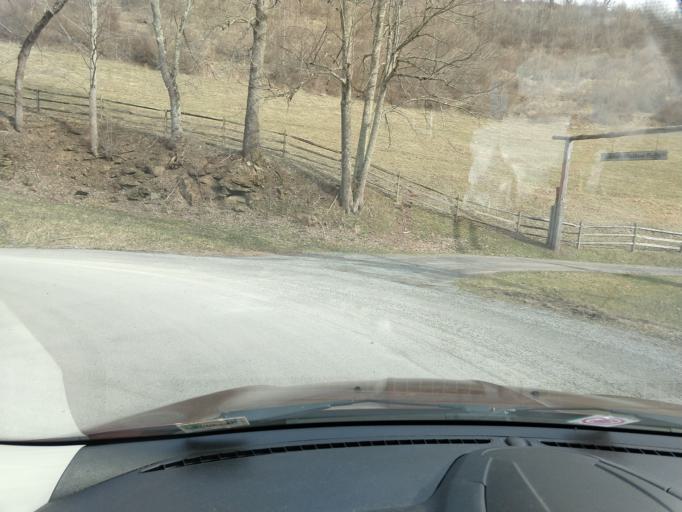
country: US
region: West Virginia
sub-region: Tucker County
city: Parsons
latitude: 39.0188
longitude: -79.5191
